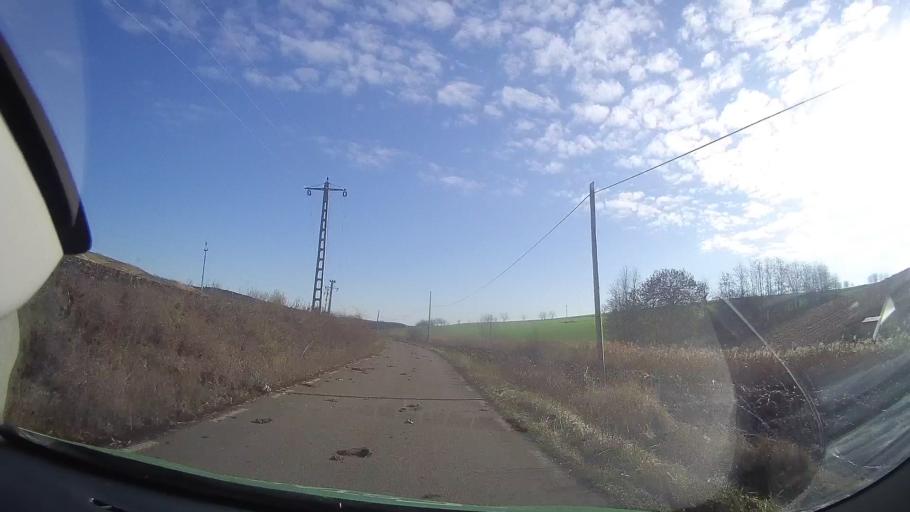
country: RO
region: Mures
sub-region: Comuna Saulia
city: Saulia
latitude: 46.6143
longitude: 24.2448
